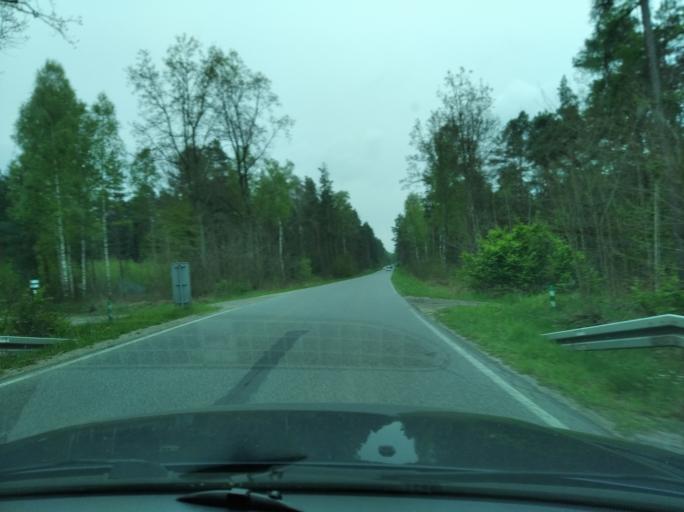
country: PL
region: Subcarpathian Voivodeship
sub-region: Powiat ropczycko-sedziszowski
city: Sedziszow Malopolski
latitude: 50.1476
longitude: 21.7578
